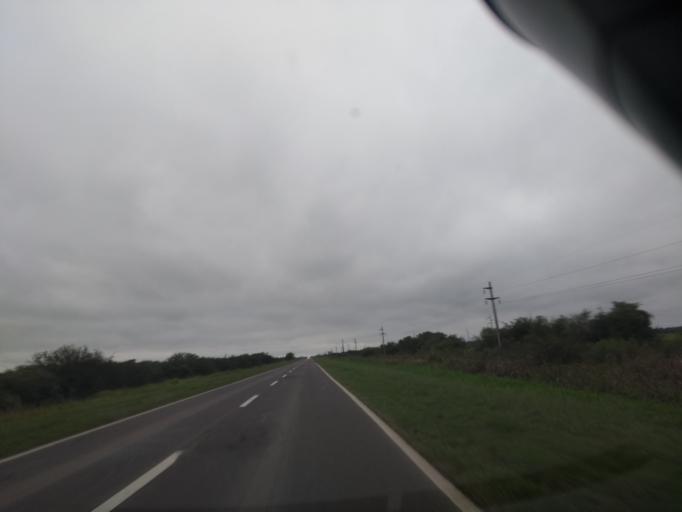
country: AR
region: Chaco
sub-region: Departamento de Quitilipi
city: Quitilipi
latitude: -26.8607
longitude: -60.2824
